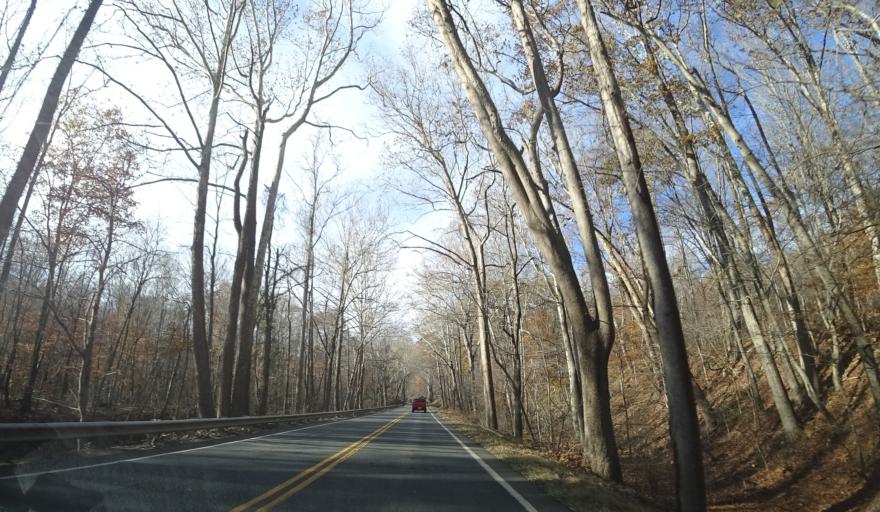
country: US
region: Virginia
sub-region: Greene County
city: Stanardsville
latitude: 38.3413
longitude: -78.5083
